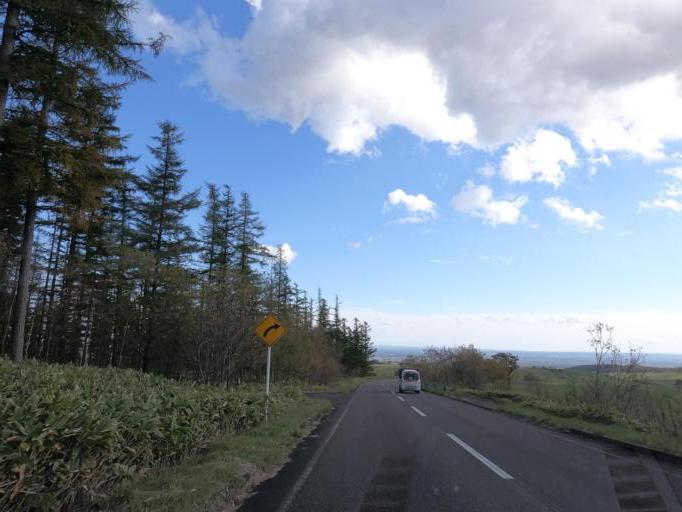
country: JP
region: Hokkaido
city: Otofuke
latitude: 43.2879
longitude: 143.2168
